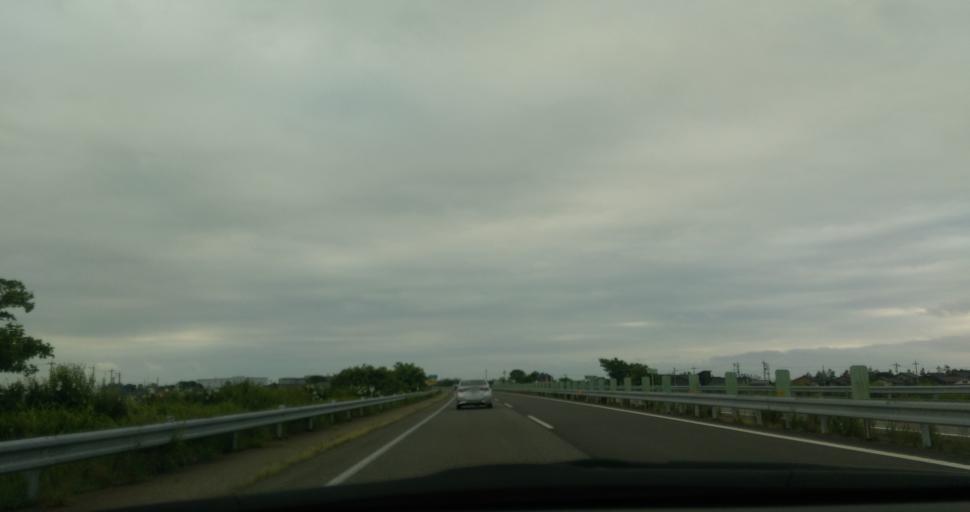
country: JP
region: Ishikawa
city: Matsuto
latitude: 36.5432
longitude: 136.5403
